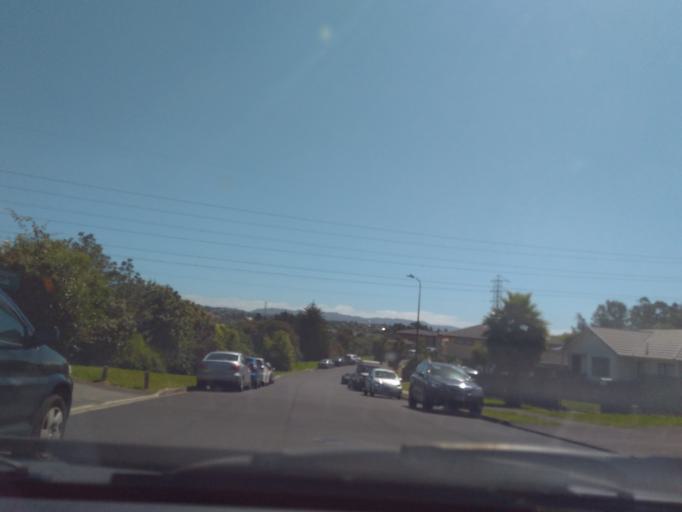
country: NZ
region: Auckland
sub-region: Auckland
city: Rosebank
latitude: -36.9011
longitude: 174.6893
